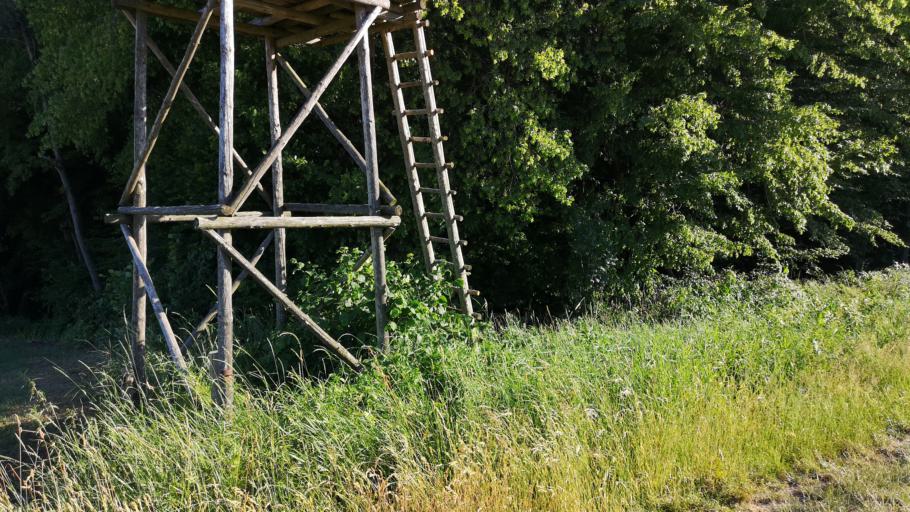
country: DE
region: Saxony-Anhalt
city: Stolberg
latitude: 51.5606
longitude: 11.0025
